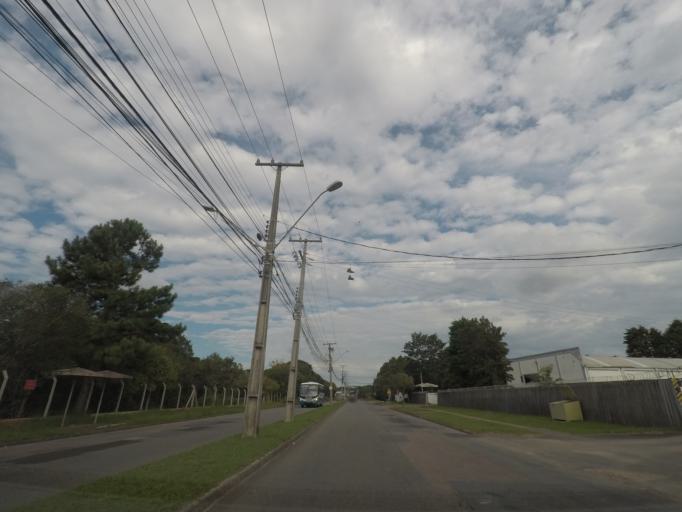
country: BR
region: Parana
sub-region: Curitiba
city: Curitiba
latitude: -25.5232
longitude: -49.3176
